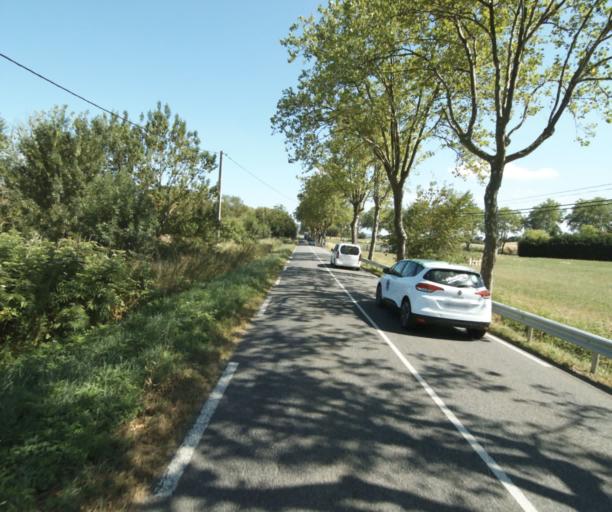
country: FR
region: Midi-Pyrenees
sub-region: Departement de la Haute-Garonne
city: Saint-Felix-Lauragais
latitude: 43.4912
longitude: 1.9030
